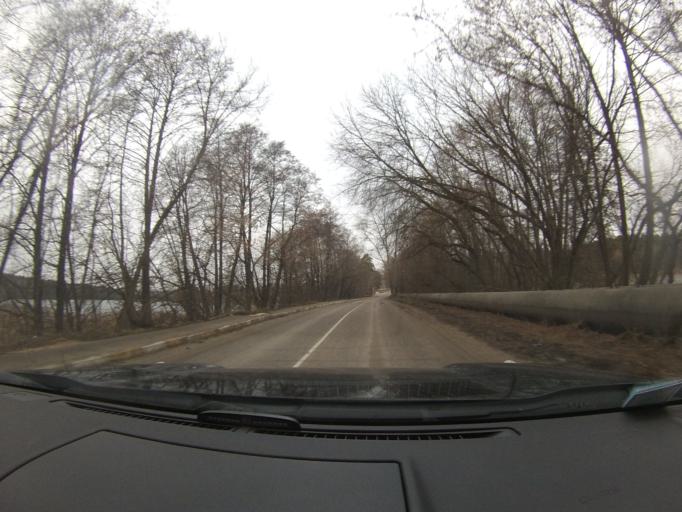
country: RU
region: Moskovskaya
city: Peski
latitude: 55.2635
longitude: 38.7603
